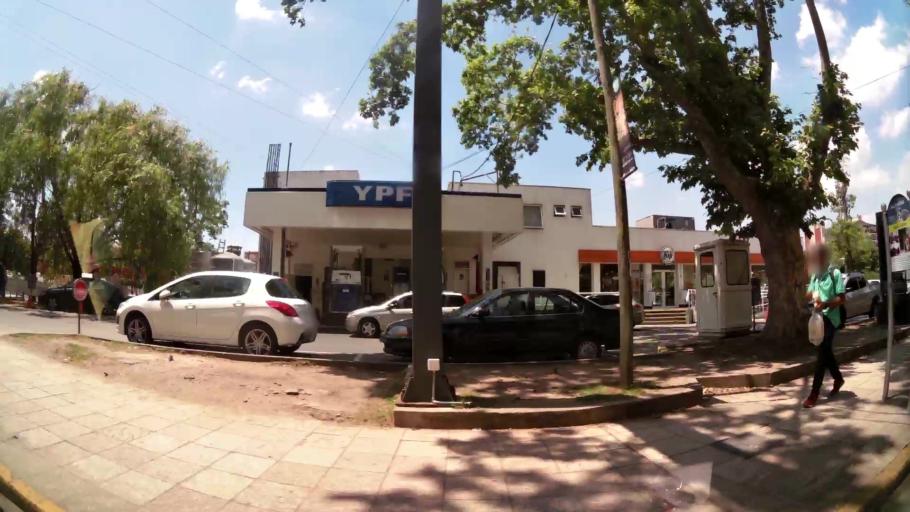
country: AR
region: Buenos Aires
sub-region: Partido de Tigre
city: Tigre
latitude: -34.4182
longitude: -58.5798
